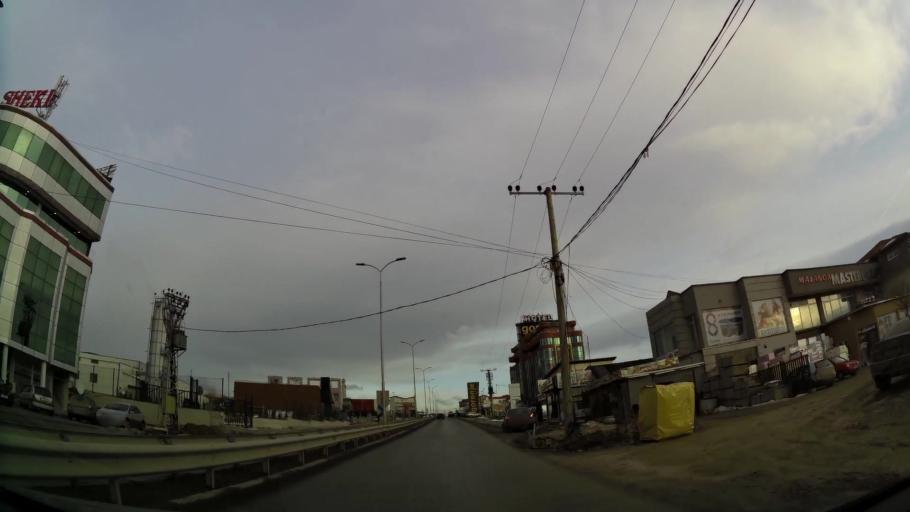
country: XK
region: Pristina
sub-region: Komuna e Prishtines
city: Pristina
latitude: 42.6305
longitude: 21.1533
